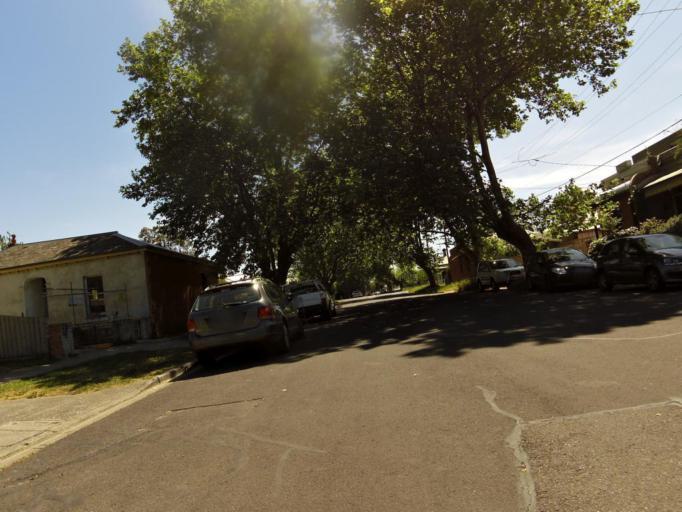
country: AU
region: Victoria
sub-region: Yarra
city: Clifton Hill
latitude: -37.7825
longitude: 144.9936
